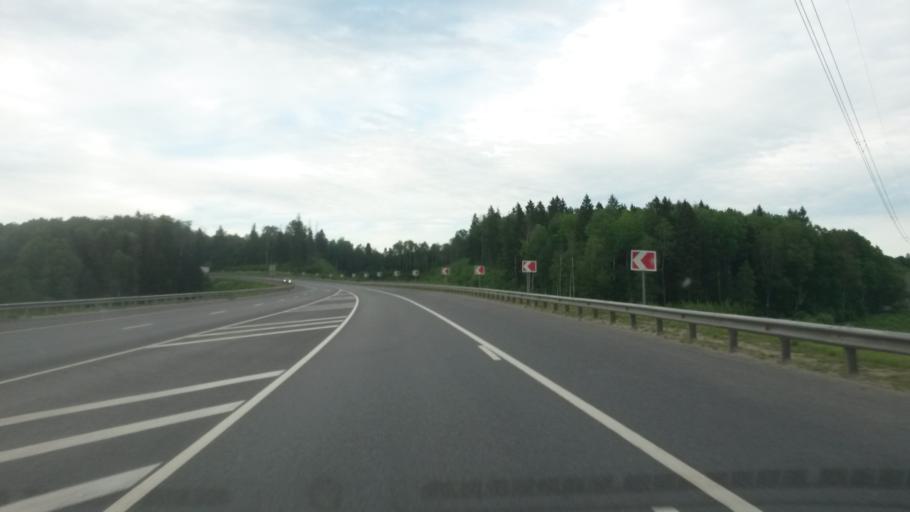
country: RU
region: Vladimir
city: Strunino
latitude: 56.5441
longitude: 38.5930
